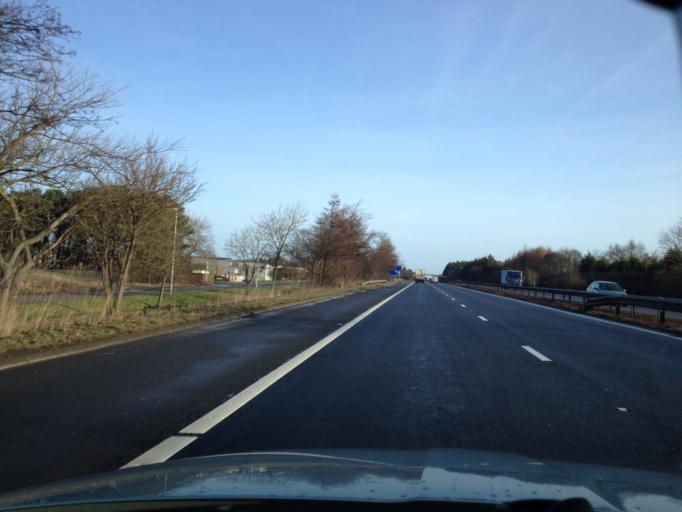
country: GB
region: Scotland
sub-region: West Lothian
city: Livingston
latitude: 55.9080
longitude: -3.5685
